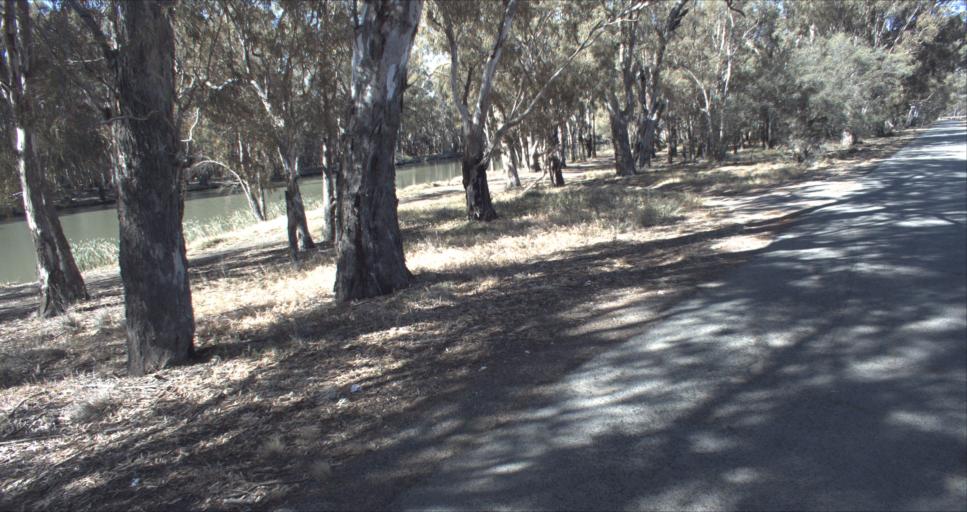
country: AU
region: New South Wales
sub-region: Leeton
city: Leeton
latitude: -34.6076
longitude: 146.2626
